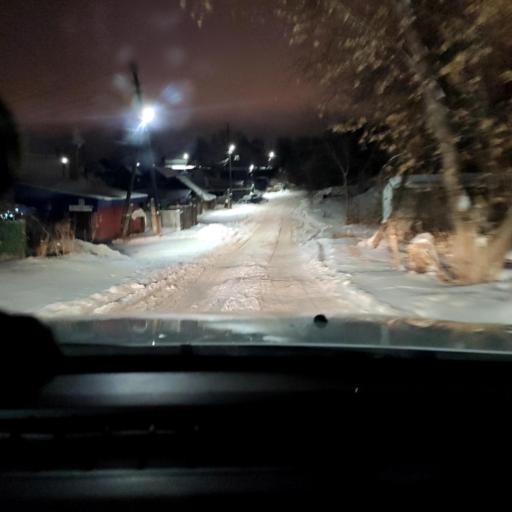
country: RU
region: Samara
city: Samara
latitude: 53.1733
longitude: 50.1674
